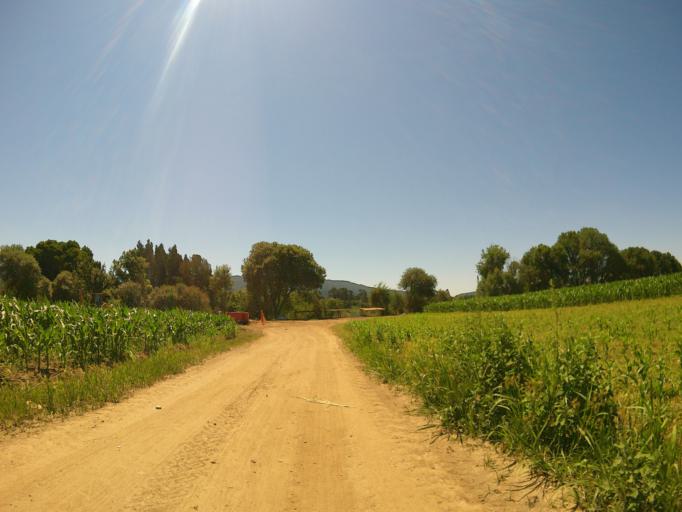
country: PT
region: Viana do Castelo
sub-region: Viana do Castelo
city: Darque
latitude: 41.7185
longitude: -8.7046
